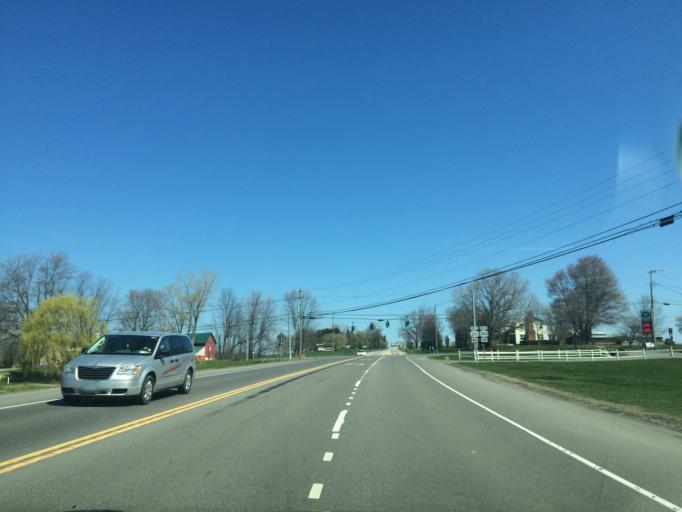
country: US
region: New York
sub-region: Wayne County
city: Macedon
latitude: 43.0929
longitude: -77.3021
